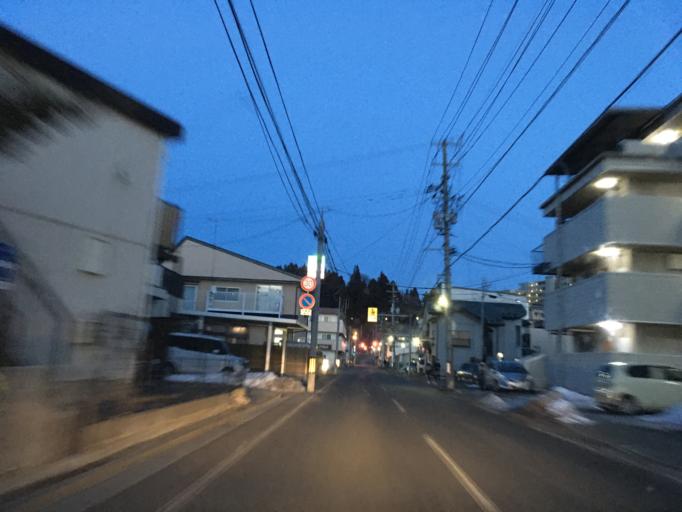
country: JP
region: Iwate
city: Morioka-shi
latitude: 39.7034
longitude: 141.1631
